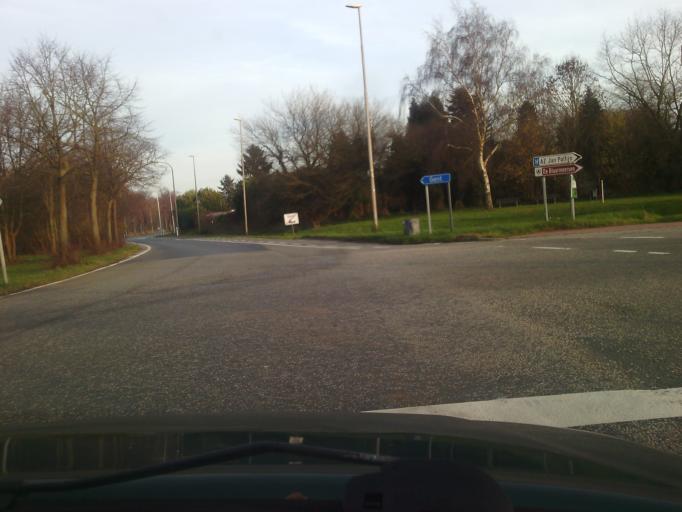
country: BE
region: Flanders
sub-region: Provincie Oost-Vlaanderen
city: Gent
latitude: 51.0533
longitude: 3.6768
